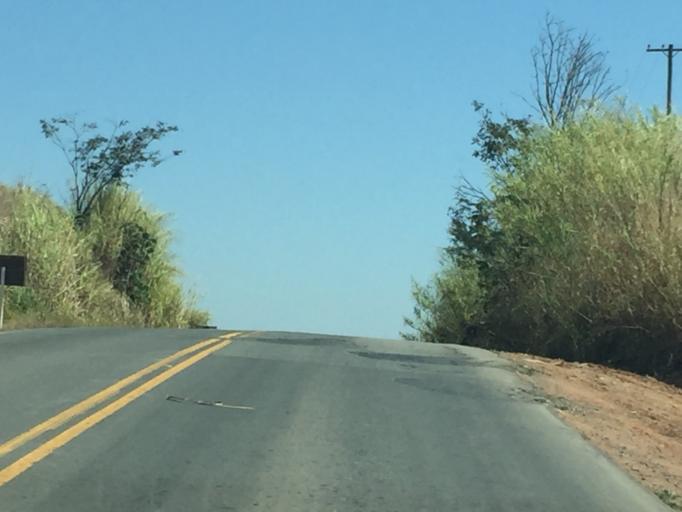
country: BR
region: Sao Paulo
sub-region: Itapira
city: Itapira
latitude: -22.3985
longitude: -46.8517
